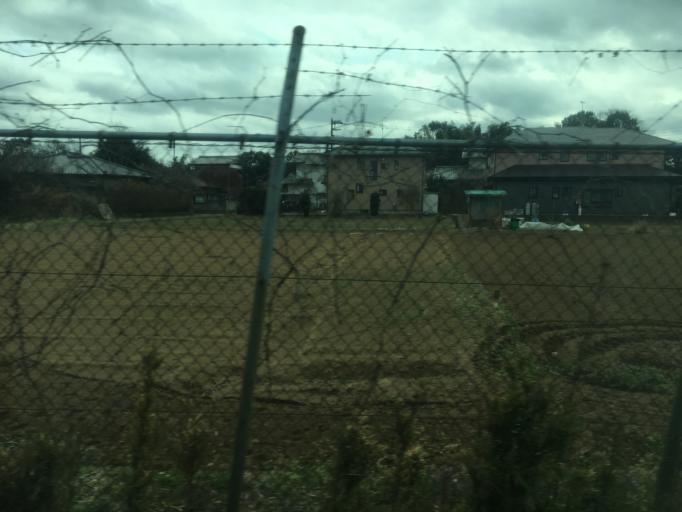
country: JP
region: Ibaraki
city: Toride
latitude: 35.8640
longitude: 140.0954
